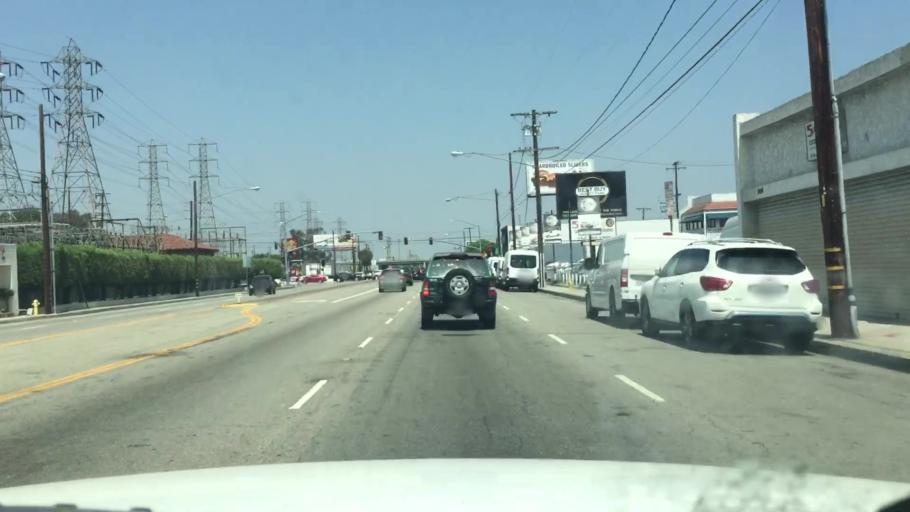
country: US
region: California
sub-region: Los Angeles County
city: Lakewood
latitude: 33.8734
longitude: -118.1425
